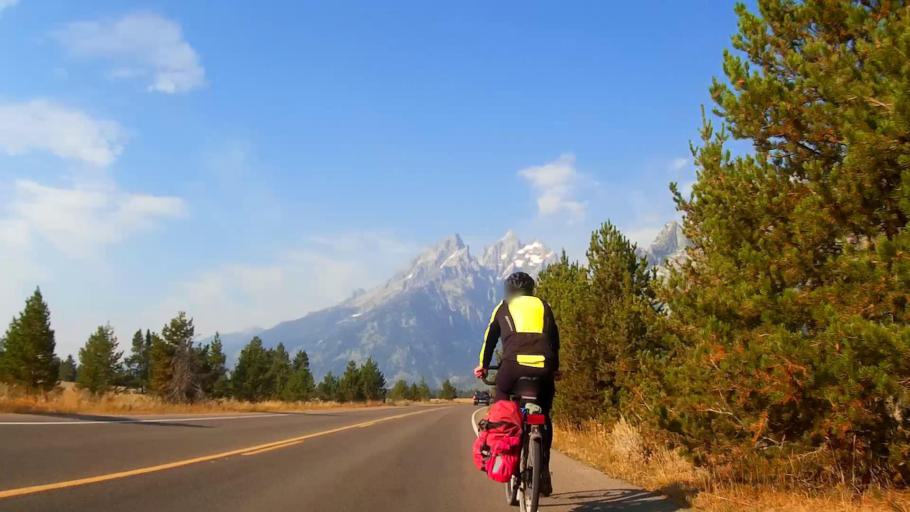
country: US
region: Wyoming
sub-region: Teton County
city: Moose Wilson Road
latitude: 43.7906
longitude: -110.7112
